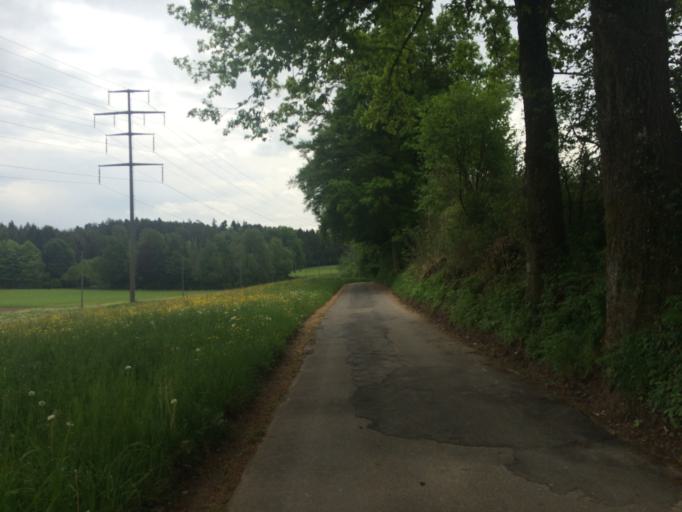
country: CH
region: Zurich
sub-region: Bezirk Uster
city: Uster / Ober-Uster
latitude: 47.3392
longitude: 8.7447
